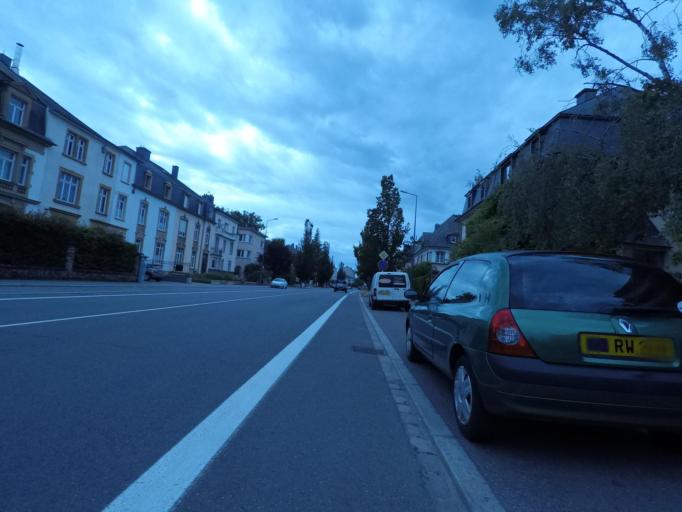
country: LU
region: Luxembourg
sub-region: Canton de Luxembourg
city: Luxembourg
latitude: 49.6069
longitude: 6.1174
